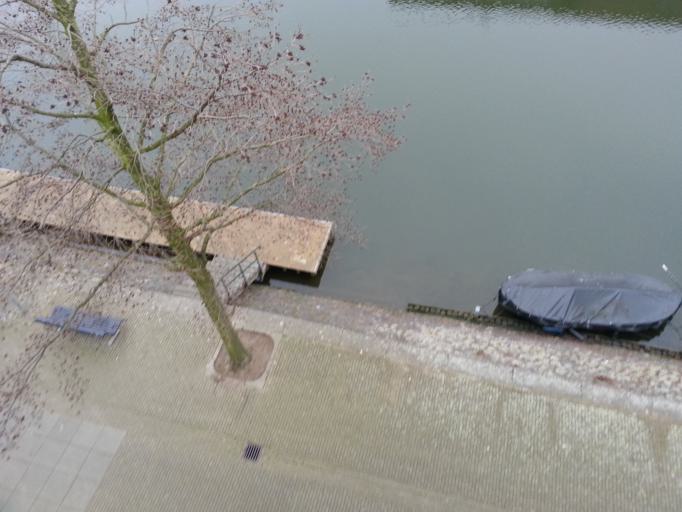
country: NL
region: North Holland
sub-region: Gemeente Diemen
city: Diemen
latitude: 52.3677
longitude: 4.9410
